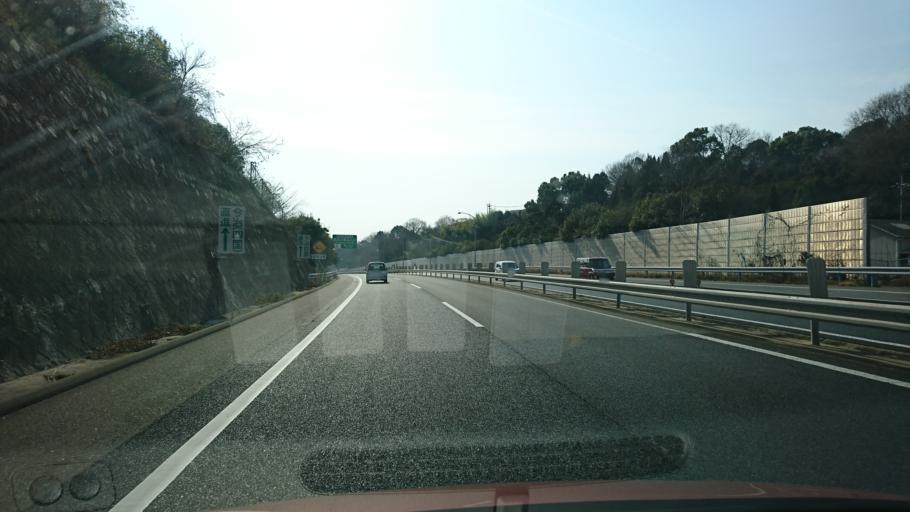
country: JP
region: Hiroshima
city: Onomichi
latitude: 34.4206
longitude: 133.2186
